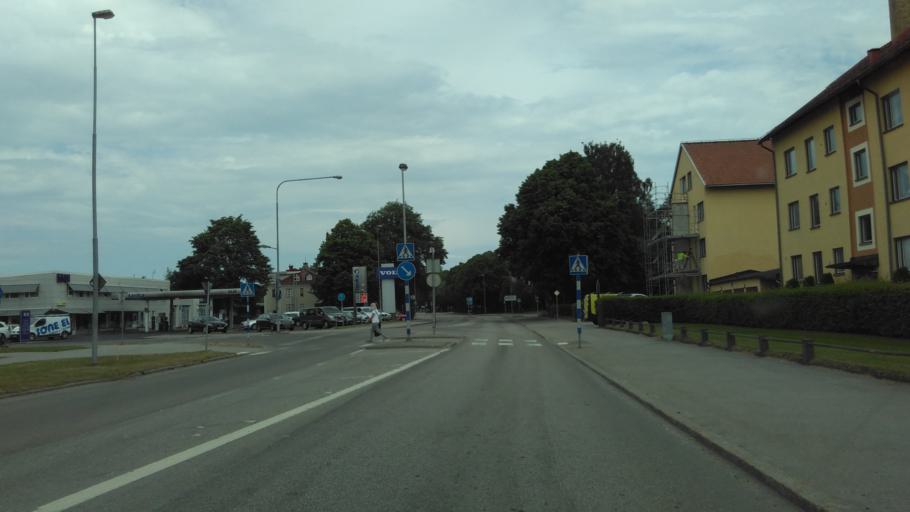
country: SE
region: Vaestra Goetaland
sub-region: Lidkopings Kommun
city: Lidkoping
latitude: 58.4955
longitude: 13.1483
